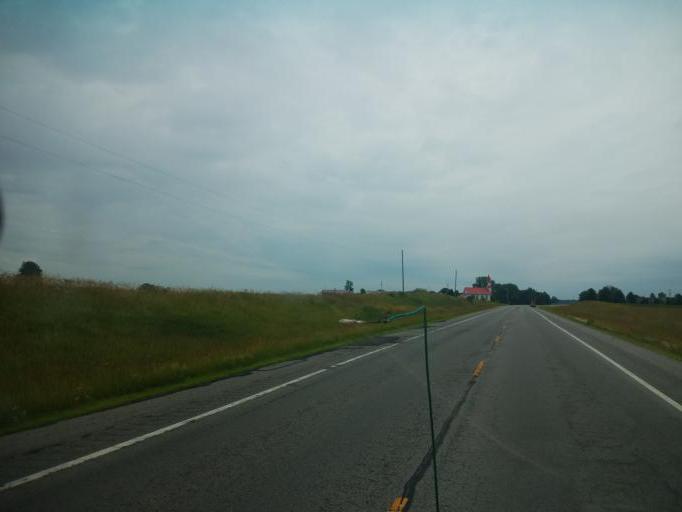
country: US
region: Ohio
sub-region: Hardin County
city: Kenton
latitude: 40.6915
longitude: -83.6964
